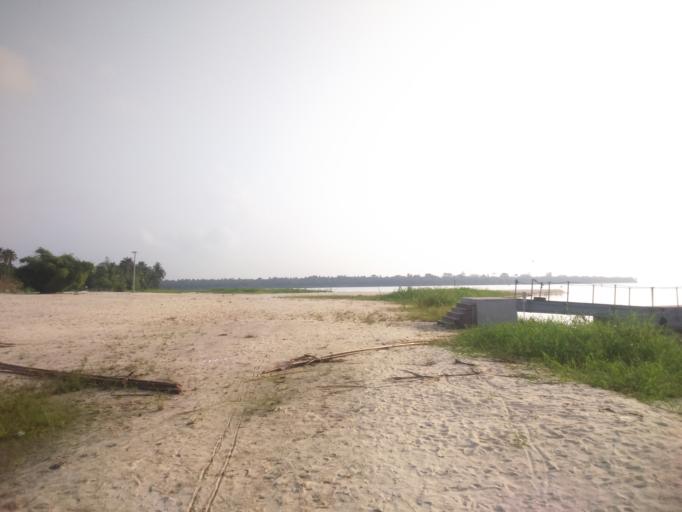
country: CI
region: Sud-Comoe
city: Adiake
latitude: 5.2866
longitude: -3.2902
